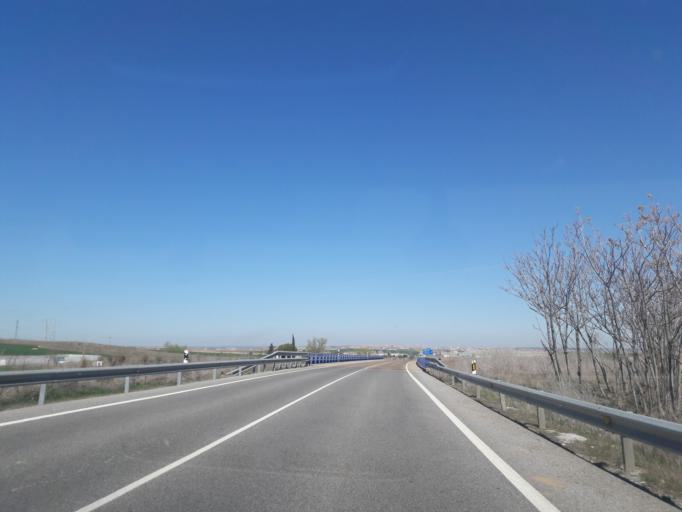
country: ES
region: Castille and Leon
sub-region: Provincia de Salamanca
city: Miranda de Azan
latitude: 40.8854
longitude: -5.6641
